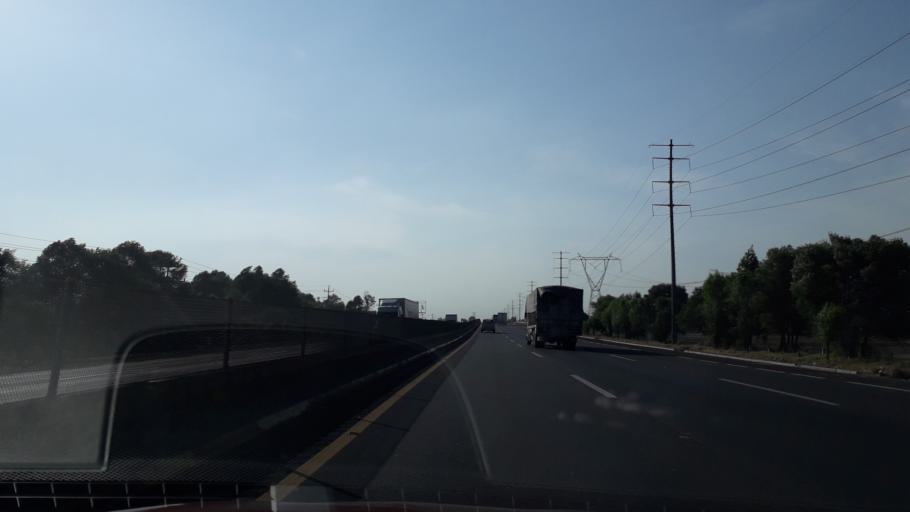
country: MX
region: Puebla
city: San Miguel Xoxtla
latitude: 19.1862
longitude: -98.3213
